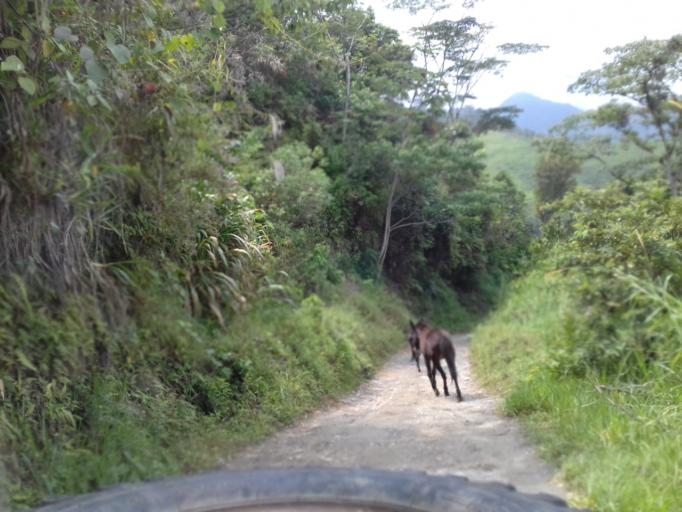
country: CO
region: Tolima
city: Libano
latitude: 4.9289
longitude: -75.0856
